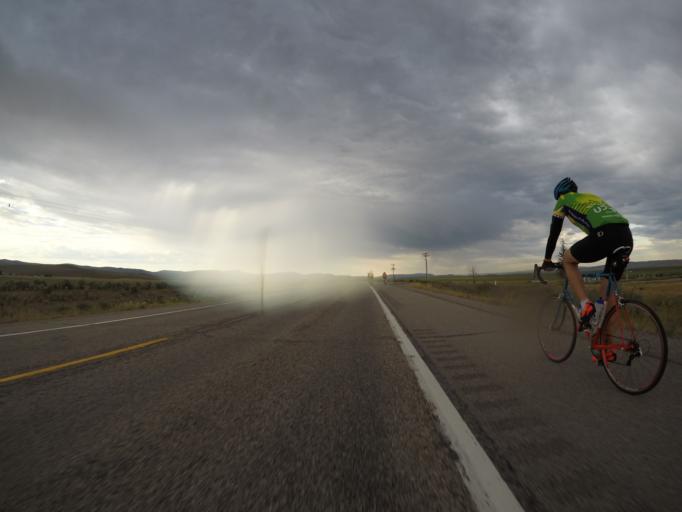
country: US
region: Utah
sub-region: Rich County
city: Randolph
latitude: 41.9331
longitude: -110.9545
